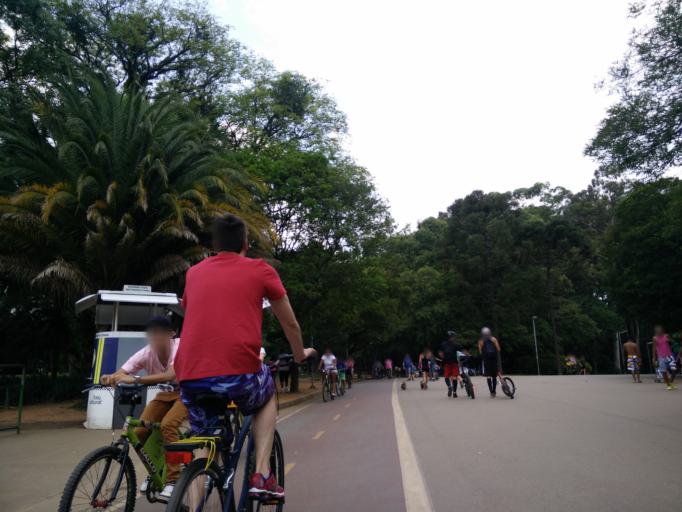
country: BR
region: Sao Paulo
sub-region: Sao Paulo
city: Sao Paulo
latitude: -23.5886
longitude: -46.6564
